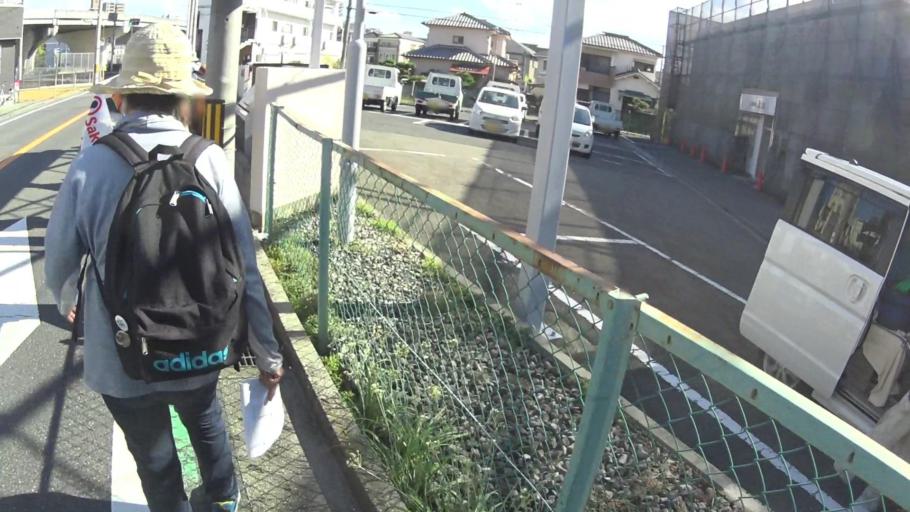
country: JP
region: Ehime
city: Kihoku-cho
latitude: 33.3990
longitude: 132.8638
